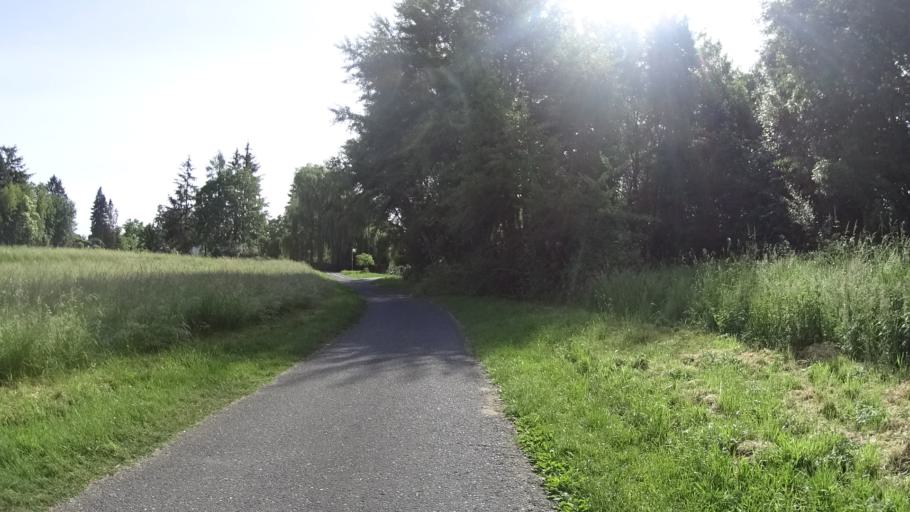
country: DE
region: Bavaria
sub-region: Regierungsbezirk Unterfranken
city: Mainaschaff
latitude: 49.9776
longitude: 9.1148
